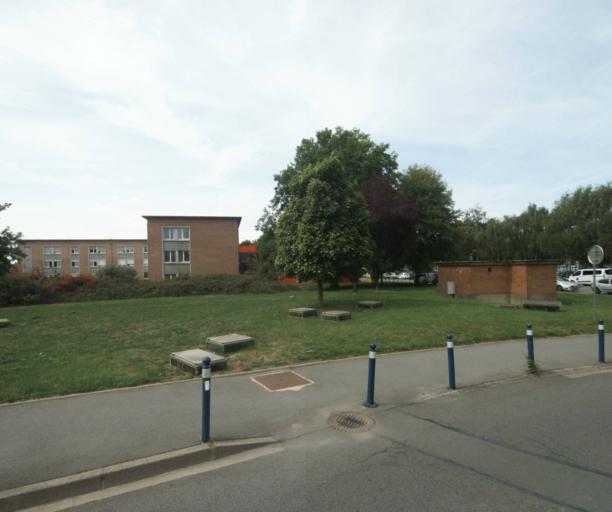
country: FR
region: Nord-Pas-de-Calais
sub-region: Departement du Nord
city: Loos
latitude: 50.6103
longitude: 3.0326
